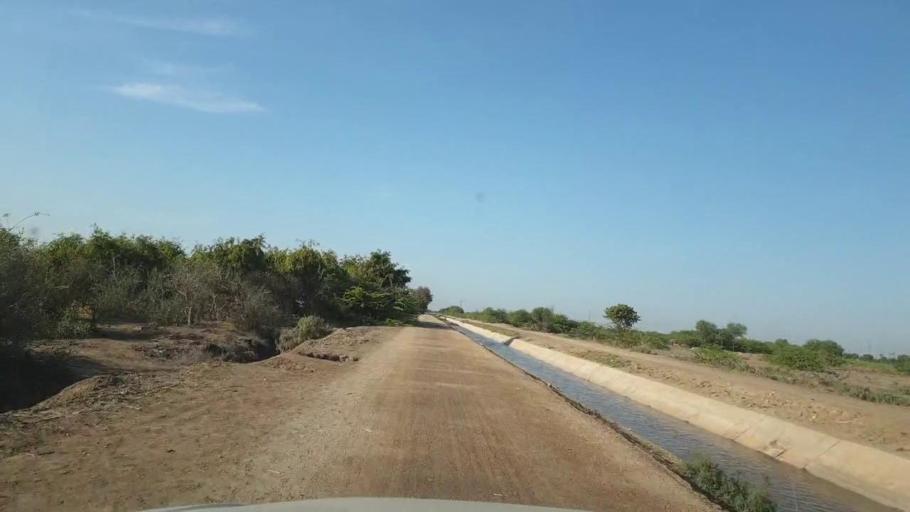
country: PK
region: Sindh
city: Kunri
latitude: 25.0923
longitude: 69.4286
